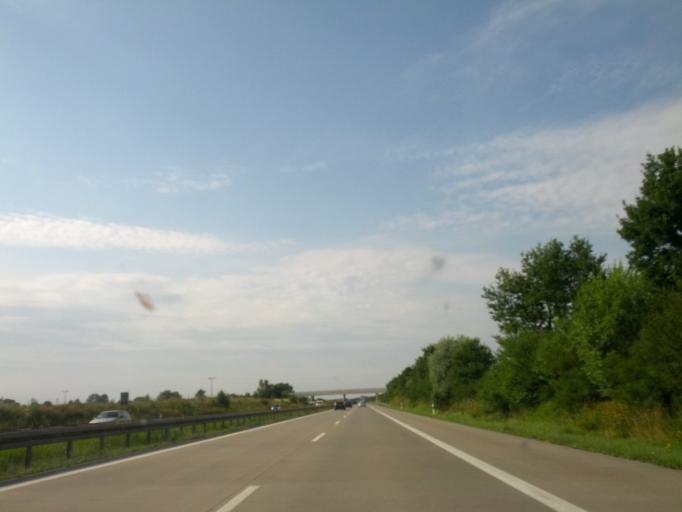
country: DE
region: Mecklenburg-Vorpommern
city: Laage
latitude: 53.9051
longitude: 12.2458
